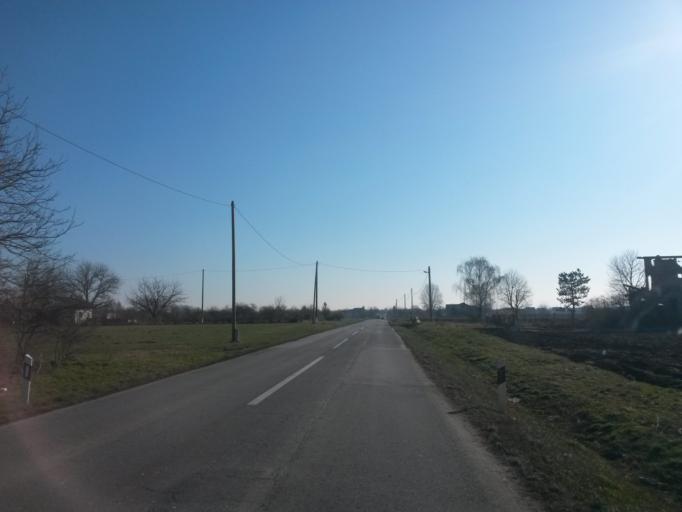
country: HR
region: Osjecko-Baranjska
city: Sarvas
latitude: 45.5197
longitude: 18.8544
